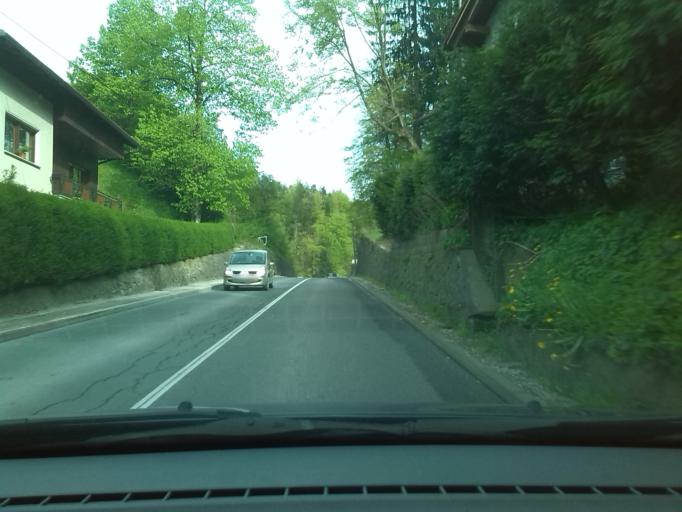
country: SI
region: Kamnik
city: Mekinje
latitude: 46.2347
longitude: 14.6644
